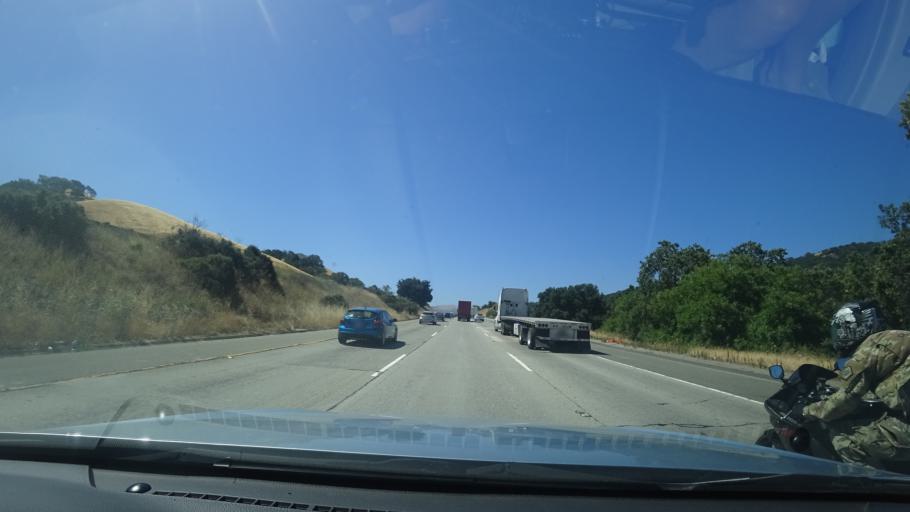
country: US
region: California
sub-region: Alameda County
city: Pleasanton
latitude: 37.6245
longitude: -121.8803
